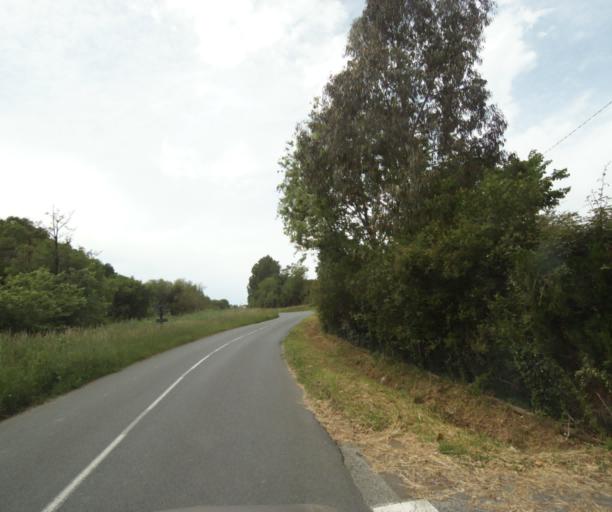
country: FR
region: Aquitaine
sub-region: Departement des Pyrenees-Atlantiques
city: Mouguerre
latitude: 43.4829
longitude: -1.4241
